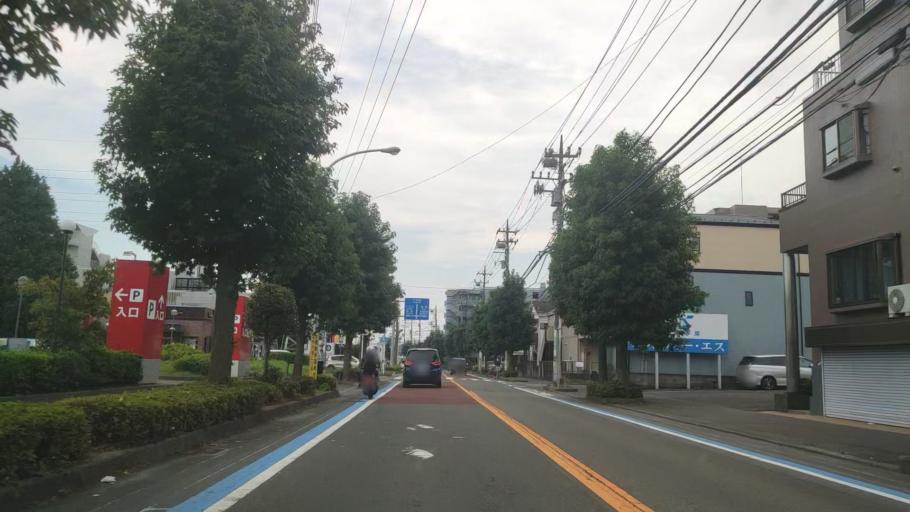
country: JP
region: Kanagawa
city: Minami-rinkan
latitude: 35.5031
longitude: 139.4493
